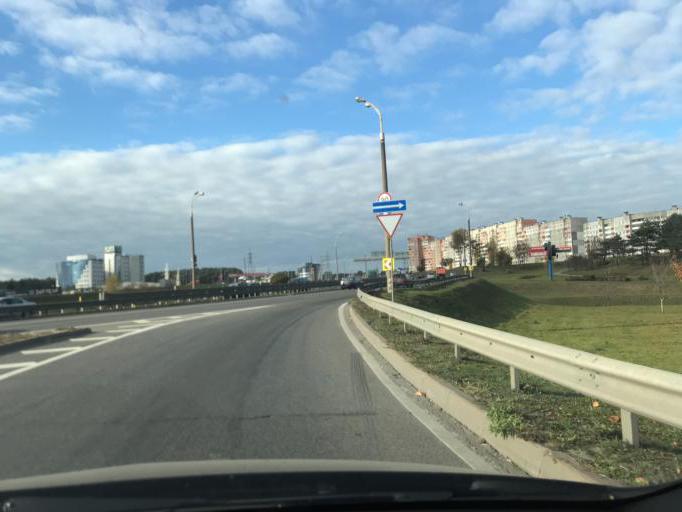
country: BY
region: Minsk
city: Borovlyany
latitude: 53.9421
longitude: 27.6729
